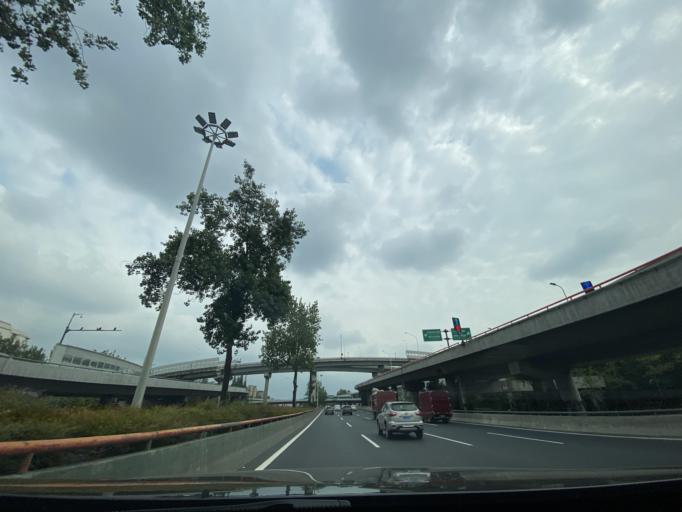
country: CN
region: Sichuan
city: Chengdu
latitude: 30.6343
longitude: 103.9950
